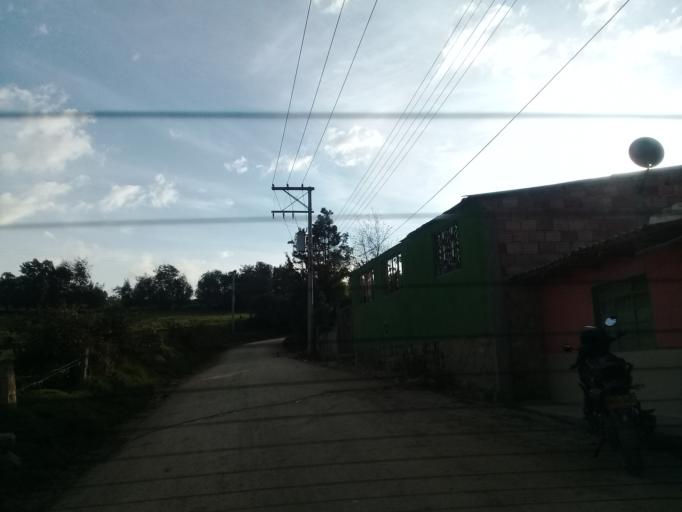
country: CO
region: Cundinamarca
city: Sibate
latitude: 4.4517
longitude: -74.2711
